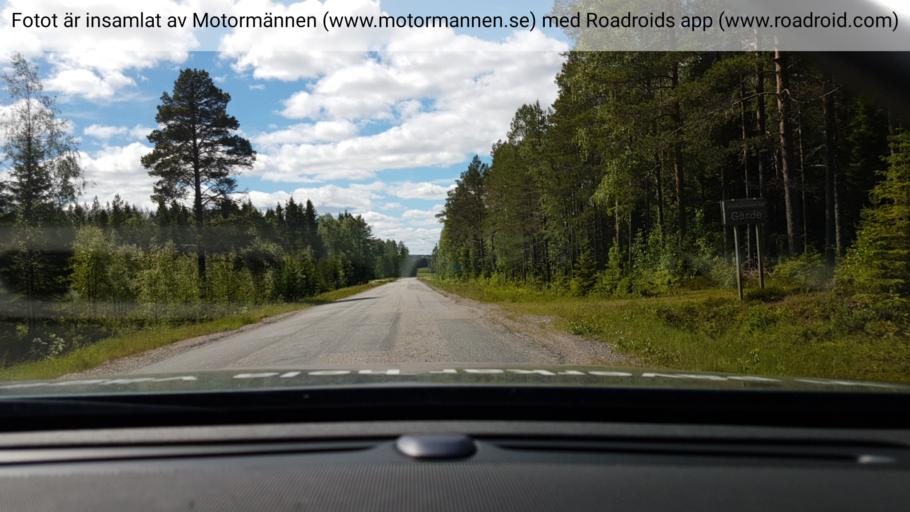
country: SE
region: Vaesterbotten
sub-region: Skelleftea Kommun
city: Burea
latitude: 64.3964
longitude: 21.3338
